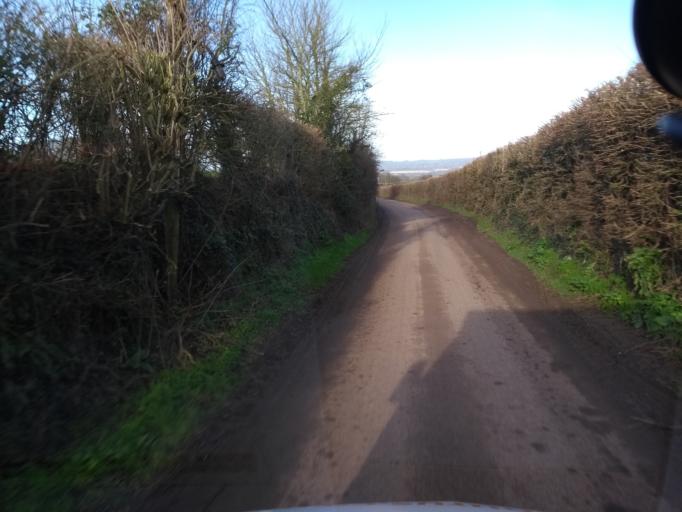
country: GB
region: England
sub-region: Somerset
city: Creech Saint Michael
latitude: 51.0180
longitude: -2.9840
